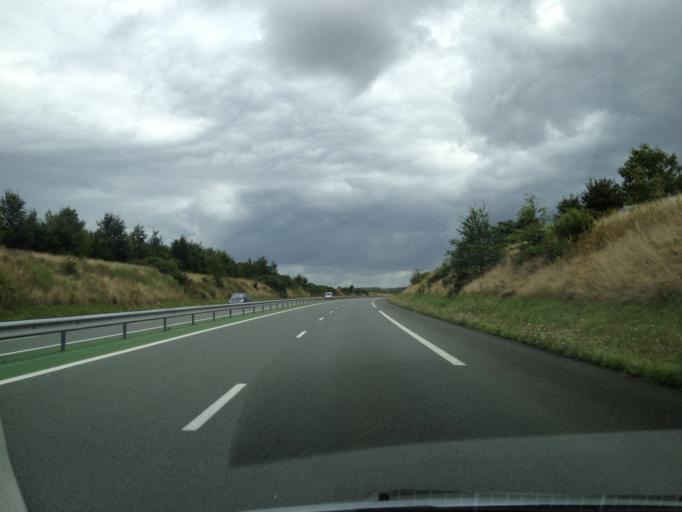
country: FR
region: Pays de la Loire
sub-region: Departement de la Vendee
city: Beaurepaire
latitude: 46.8876
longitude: -1.1006
